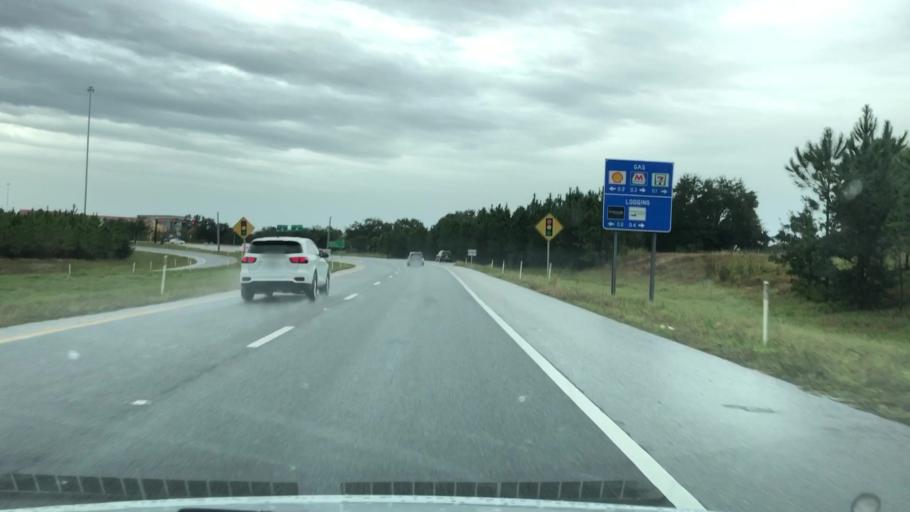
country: US
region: Florida
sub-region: Seminole County
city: Heathrow
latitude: 28.7537
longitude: -81.3618
